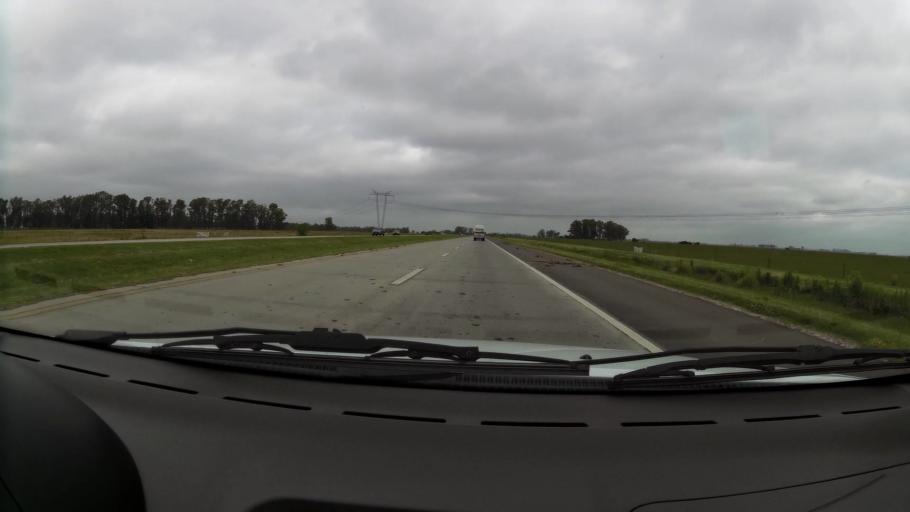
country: AR
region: Buenos Aires
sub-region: Partido de Brandsen
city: Brandsen
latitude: -35.0244
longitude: -58.2434
